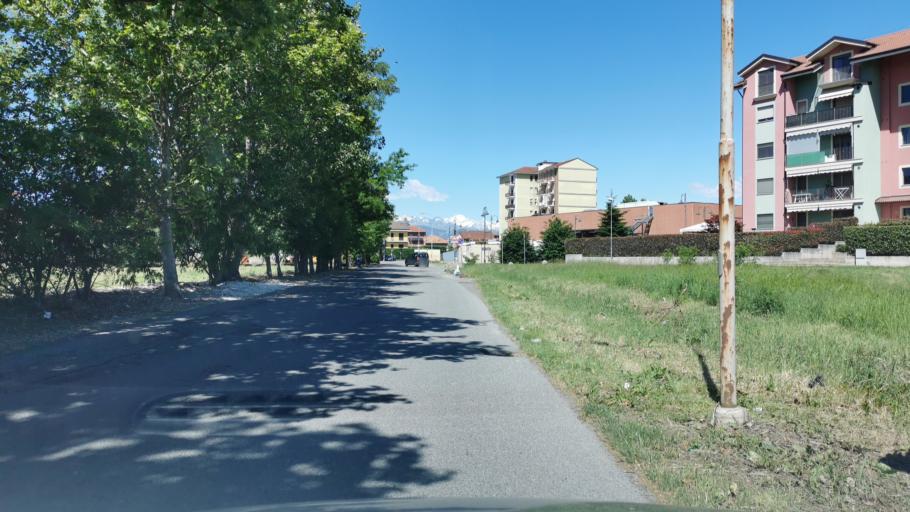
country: IT
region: Piedmont
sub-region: Provincia di Torino
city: Leini
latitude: 45.1785
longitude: 7.7182
